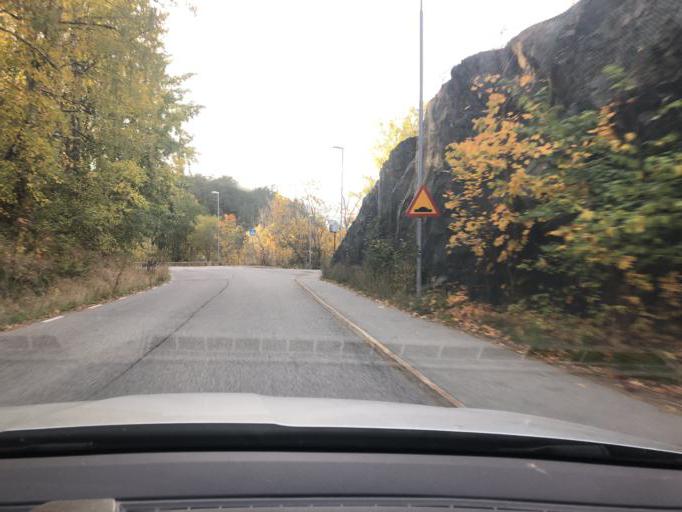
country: SE
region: Stockholm
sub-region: Nacka Kommun
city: Nacka
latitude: 59.2993
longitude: 18.1525
